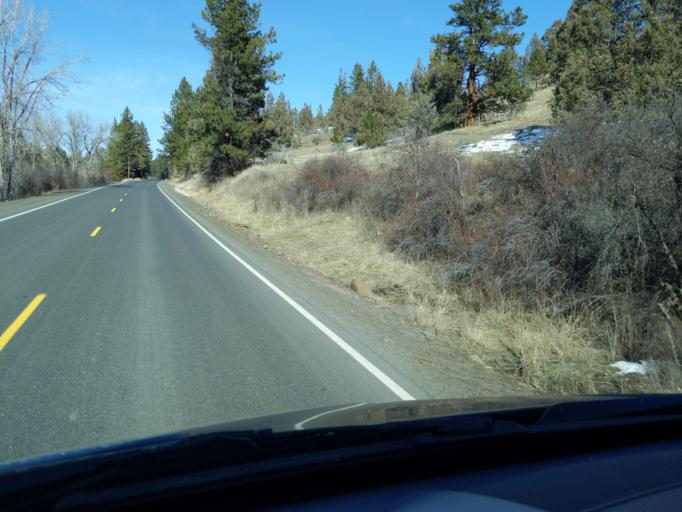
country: US
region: Oregon
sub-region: Grant County
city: John Day
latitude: 44.8618
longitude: -119.0265
